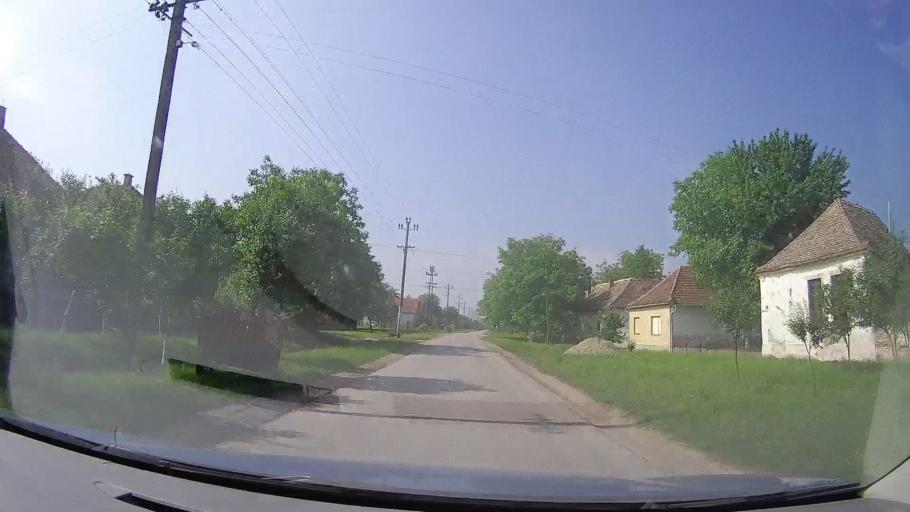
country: RS
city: Jasa Tomic
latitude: 45.4430
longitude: 20.8522
